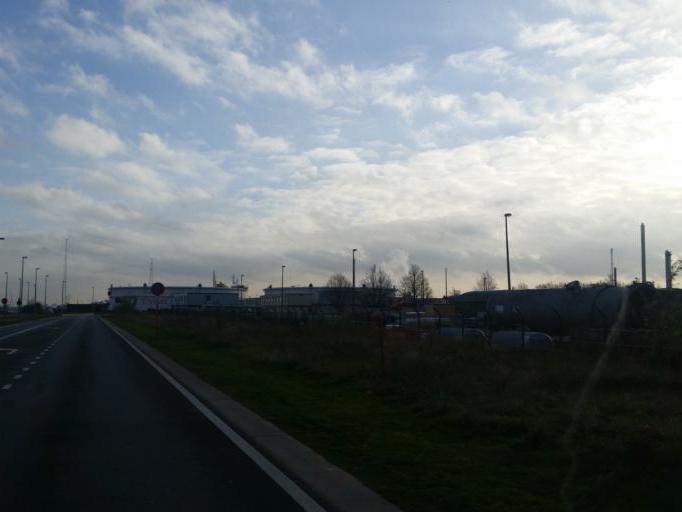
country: BE
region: Flanders
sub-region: Provincie Antwerpen
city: Zwijndrecht
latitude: 51.2760
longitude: 4.3281
